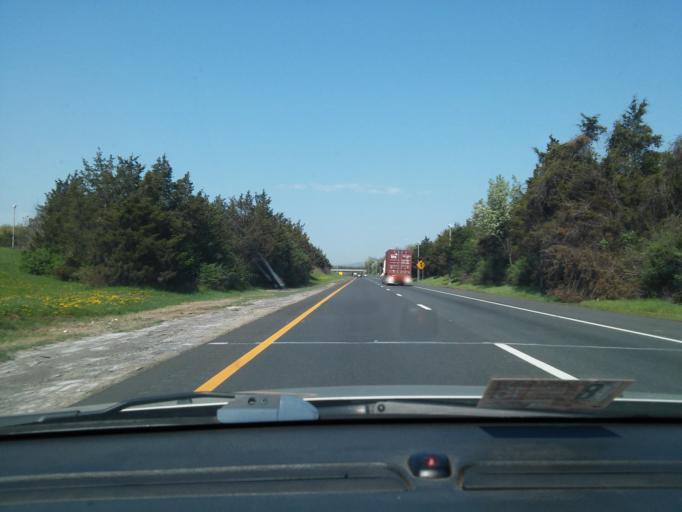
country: US
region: New Jersey
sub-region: Somerset County
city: Bedminster
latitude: 40.6432
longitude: -74.6480
